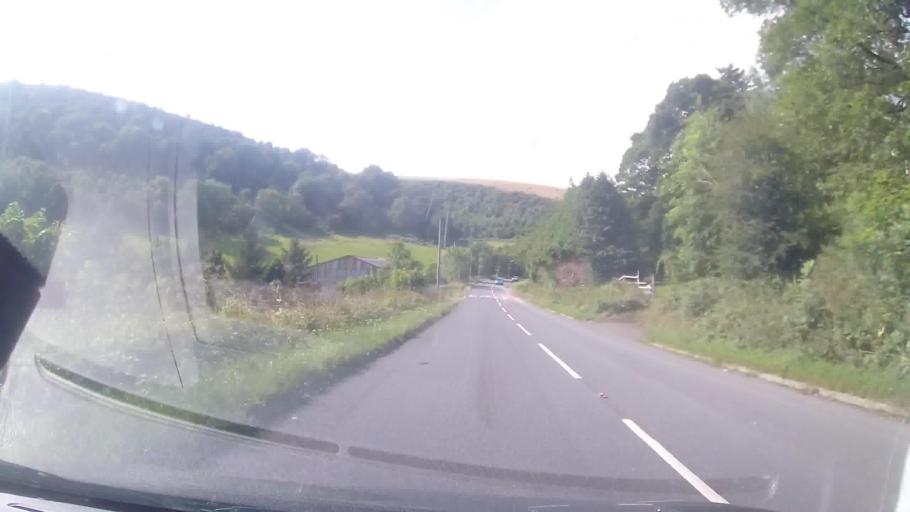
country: GB
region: Wales
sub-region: Sir Powys
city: Knighton
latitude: 52.3594
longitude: -3.0446
